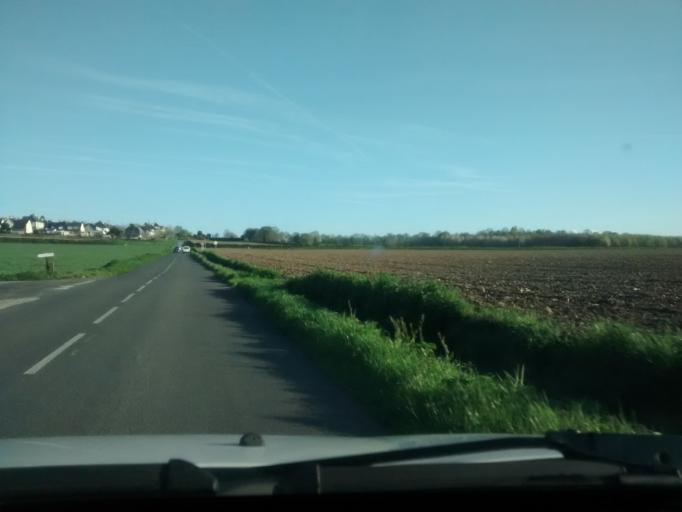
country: FR
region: Brittany
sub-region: Departement d'Ille-et-Vilaine
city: Pleine-Fougeres
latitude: 48.5473
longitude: -1.5781
